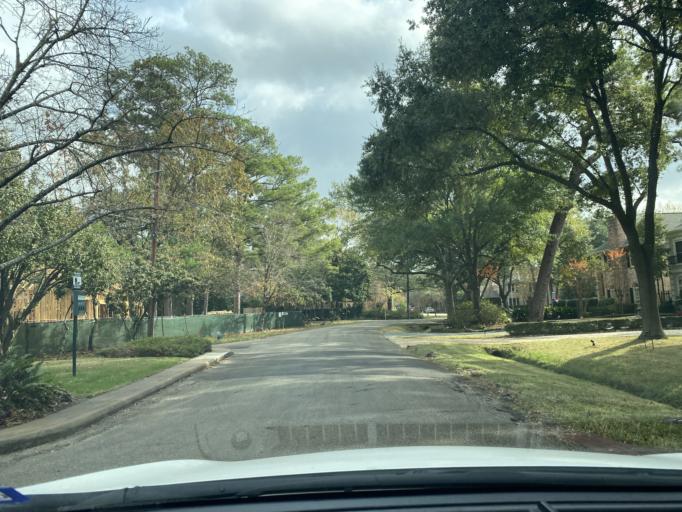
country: US
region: Texas
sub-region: Harris County
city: Hunters Creek Village
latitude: 29.7658
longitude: -95.4734
